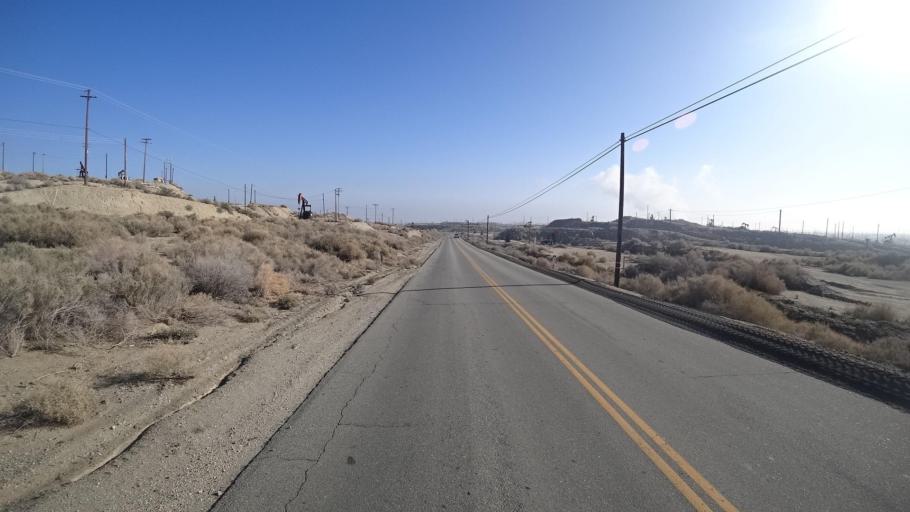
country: US
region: California
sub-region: Kern County
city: Taft Heights
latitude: 35.2195
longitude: -119.6031
